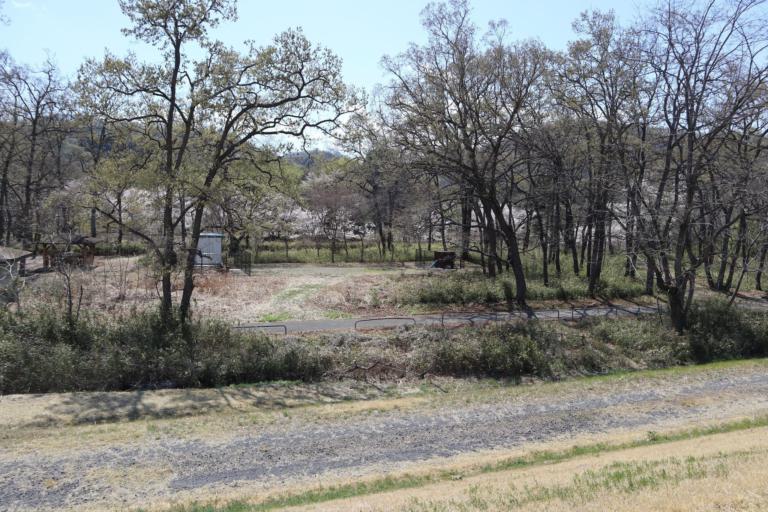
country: JP
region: Gunma
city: Kiryu
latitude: 36.3617
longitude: 139.3726
